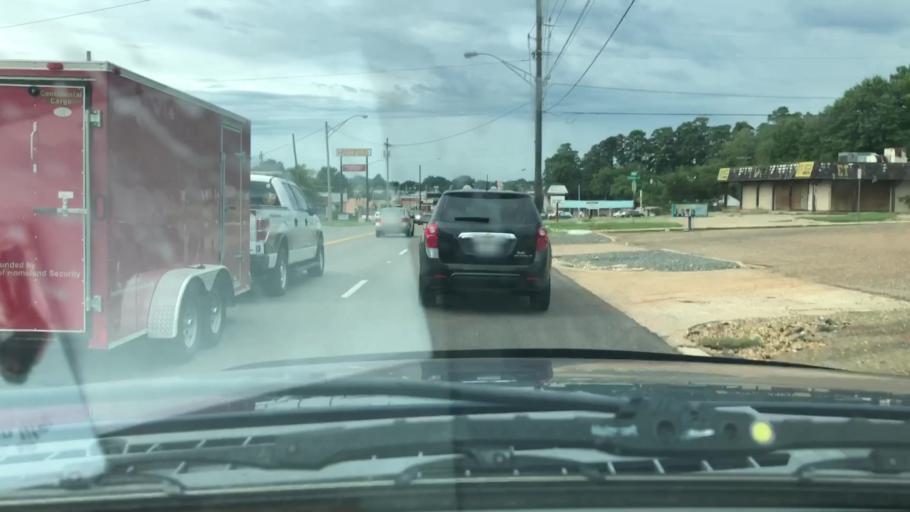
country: US
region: Texas
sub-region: Bowie County
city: Texarkana
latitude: 33.4352
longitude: -94.0712
